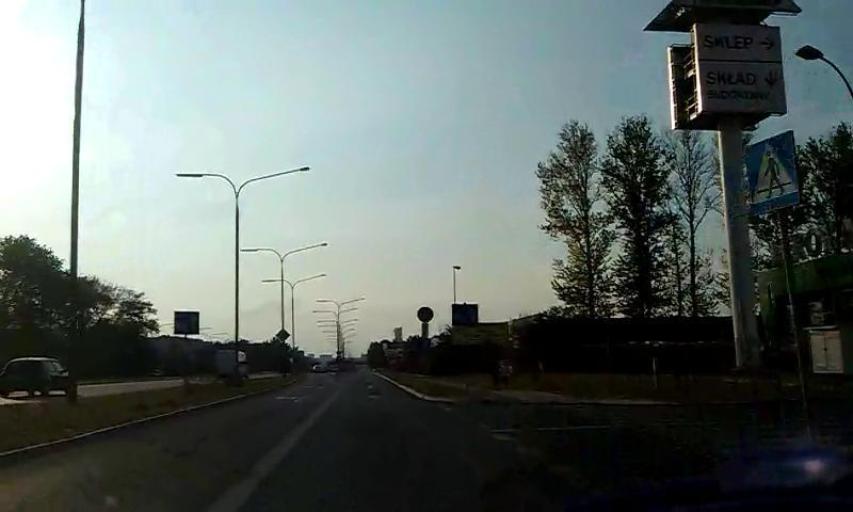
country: PL
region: Lublin Voivodeship
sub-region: Powiat lubelski
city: Jakubowice Murowane
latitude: 51.2316
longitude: 22.6103
